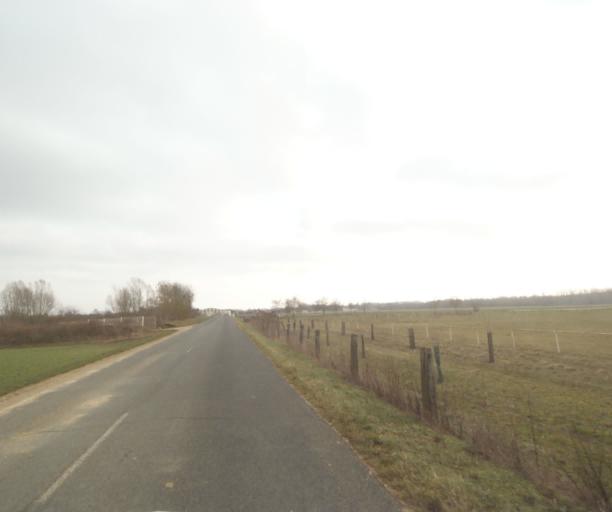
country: FR
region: Champagne-Ardenne
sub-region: Departement de la Haute-Marne
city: Villiers-en-Lieu
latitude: 48.6518
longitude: 4.8041
